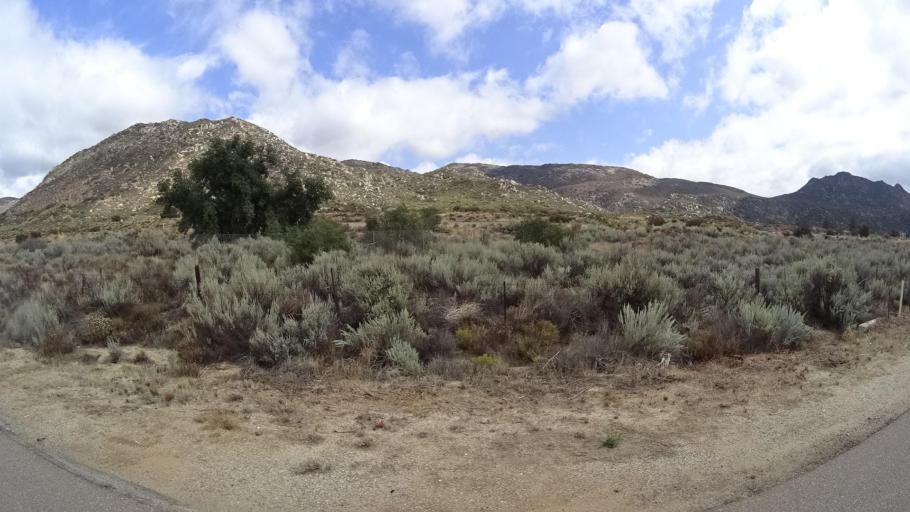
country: US
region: California
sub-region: San Diego County
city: Pine Valley
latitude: 32.7434
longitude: -116.4814
